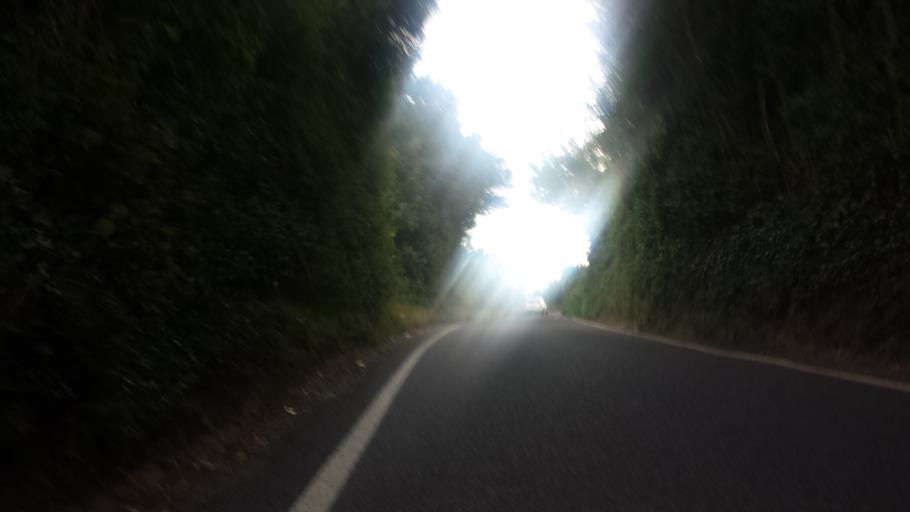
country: GB
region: England
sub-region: Kent
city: Swanley
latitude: 51.3858
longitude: 0.1871
